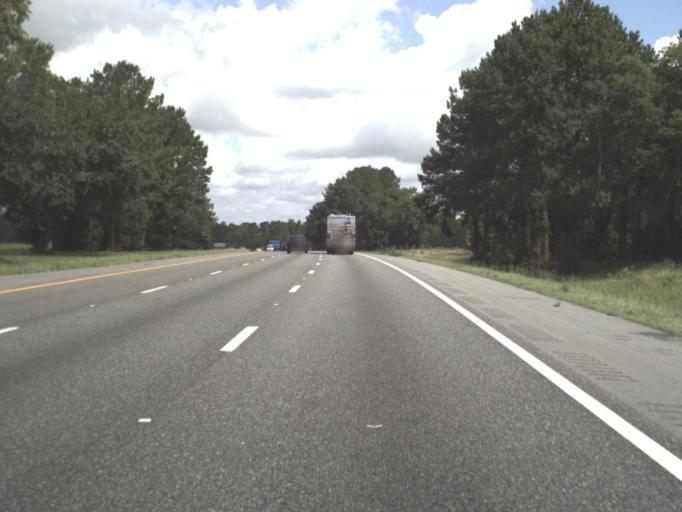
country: US
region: Florida
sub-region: Alachua County
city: High Springs
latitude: 29.9911
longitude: -82.5838
